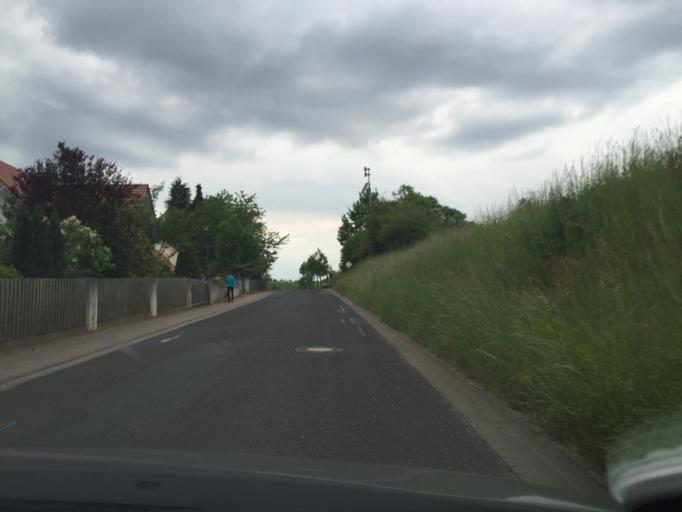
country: DE
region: Bavaria
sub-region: Regierungsbezirk Unterfranken
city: Johannesberg
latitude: 50.0316
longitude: 9.1615
